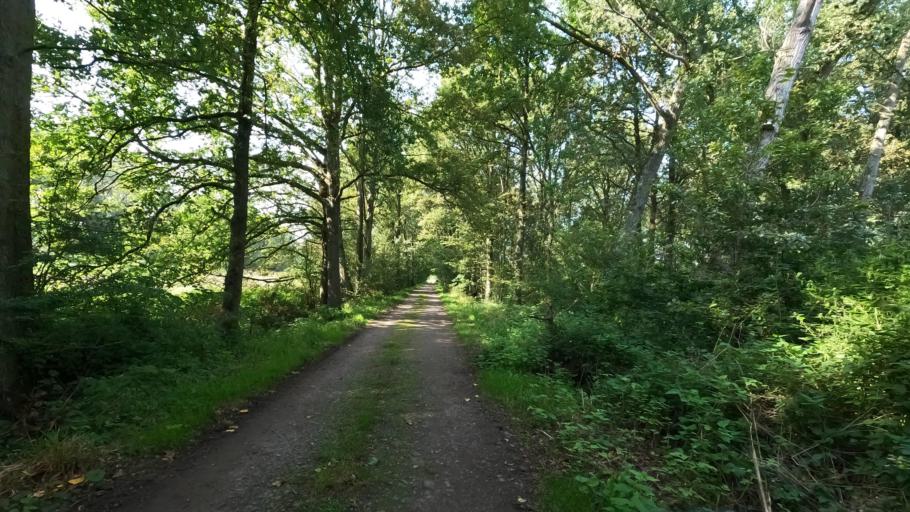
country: BE
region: Flanders
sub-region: Provincie Vlaams-Brabant
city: Boortmeerbeek
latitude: 50.9883
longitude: 4.5844
